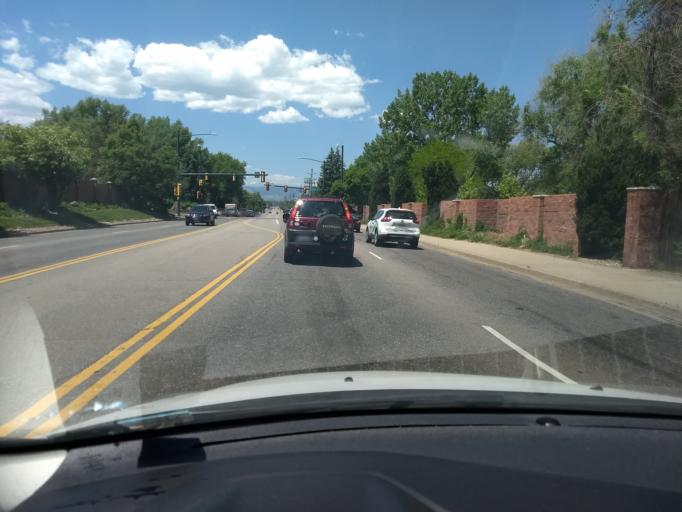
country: US
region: Colorado
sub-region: Arapahoe County
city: Cherry Hills Village
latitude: 39.6241
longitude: -104.9775
